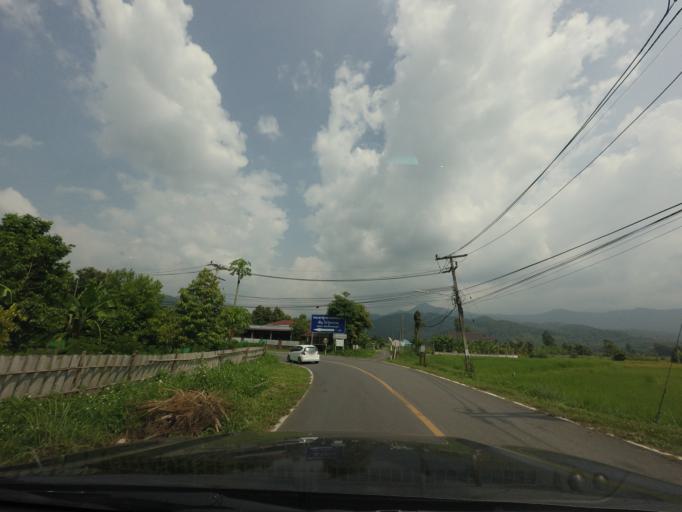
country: TH
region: Nan
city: Pua
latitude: 19.1744
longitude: 100.9415
